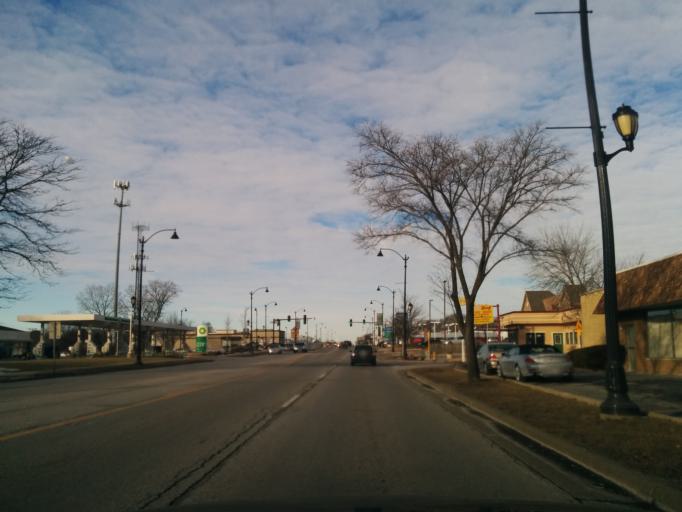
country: US
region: Illinois
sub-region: DuPage County
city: Glen Ellyn
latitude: 41.8594
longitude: -88.0745
